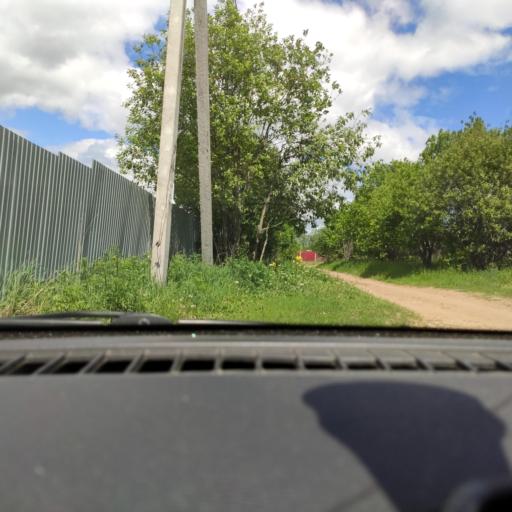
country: RU
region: Perm
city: Kondratovo
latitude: 58.0883
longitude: 56.0127
